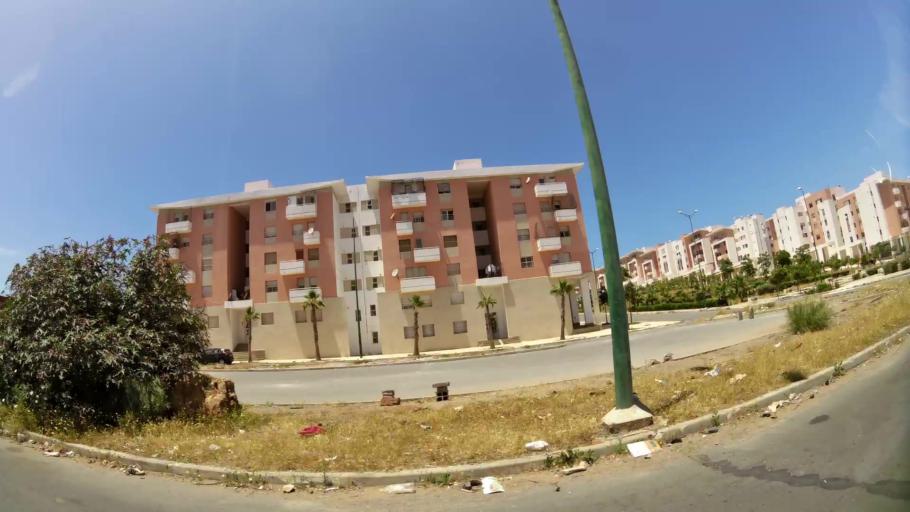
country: MA
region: Gharb-Chrarda-Beni Hssen
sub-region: Kenitra Province
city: Kenitra
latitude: 34.2492
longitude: -6.6498
